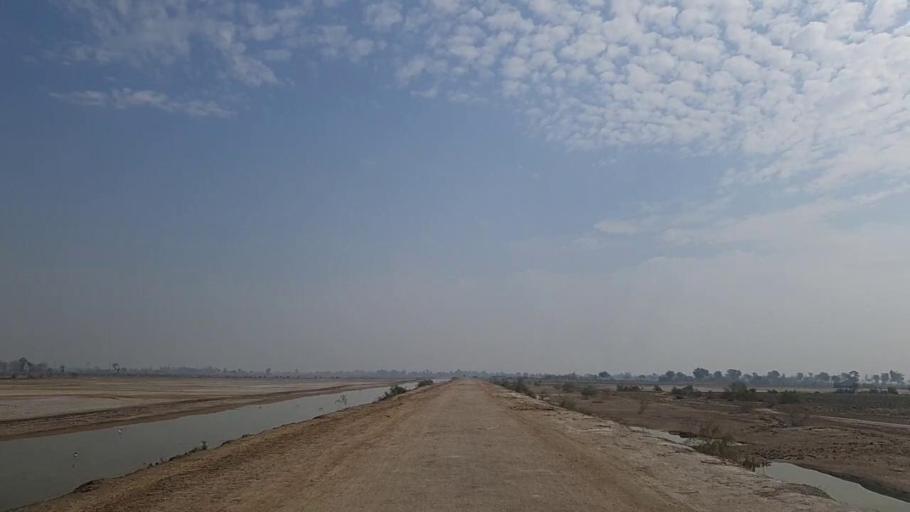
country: PK
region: Sindh
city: Daur
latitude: 26.3841
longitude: 68.3773
